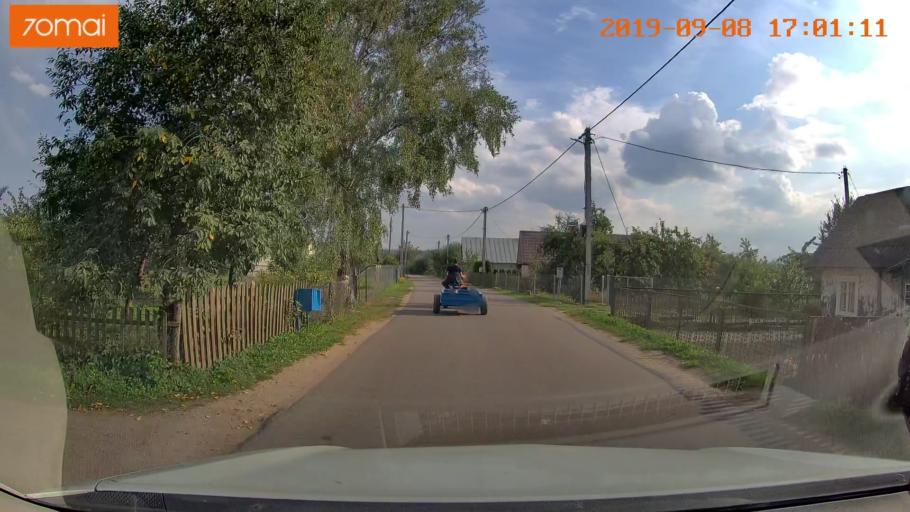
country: BY
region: Grodnenskaya
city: Hrodna
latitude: 53.7115
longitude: 23.9339
